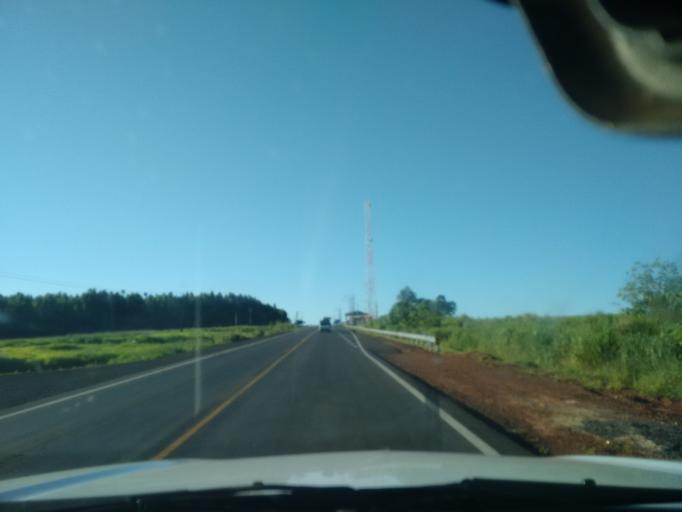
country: BR
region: Mato Grosso do Sul
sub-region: Eldorado
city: Eldorado
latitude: -23.8711
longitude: -54.3257
